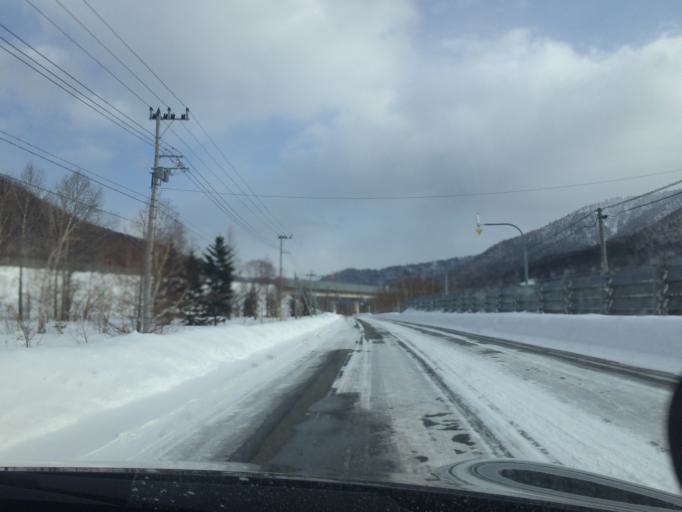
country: JP
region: Hokkaido
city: Shimo-furano
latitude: 43.0605
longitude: 142.5589
